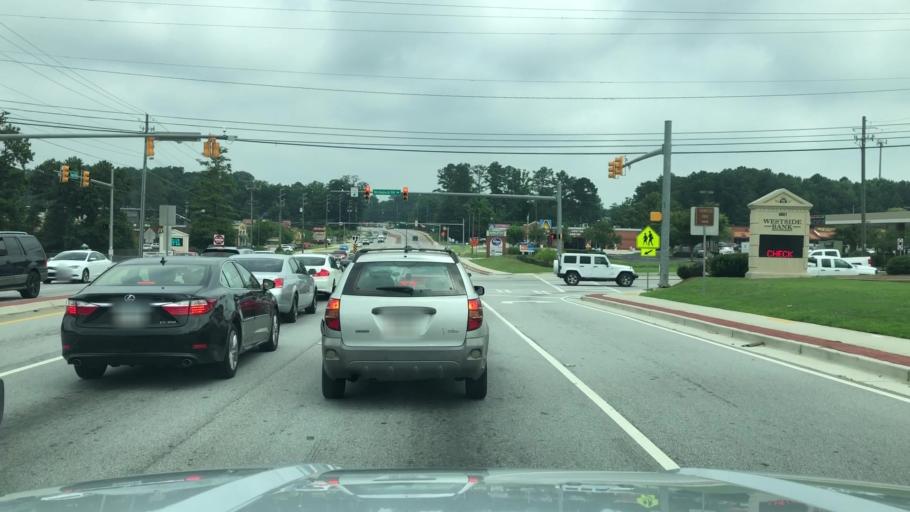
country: US
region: Georgia
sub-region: Cobb County
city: Mableton
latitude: 33.8337
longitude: -84.5759
